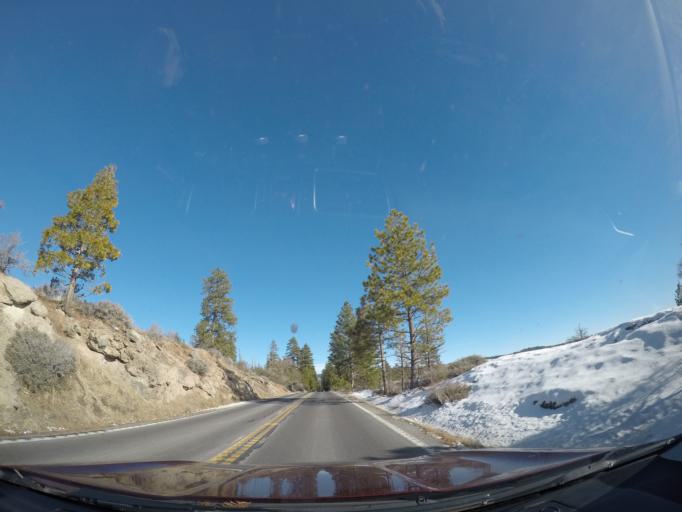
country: US
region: California
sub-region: Tuolumne County
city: Twain Harte
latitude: 38.1474
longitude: -120.0787
